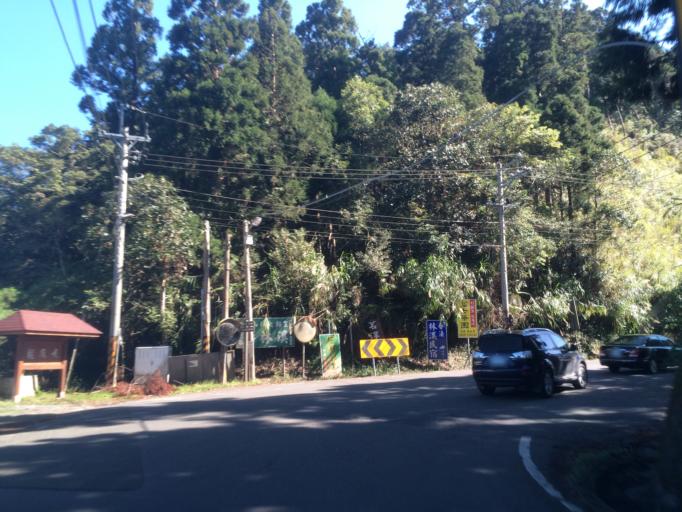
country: TW
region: Taiwan
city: Lugu
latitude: 23.6555
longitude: 120.7829
